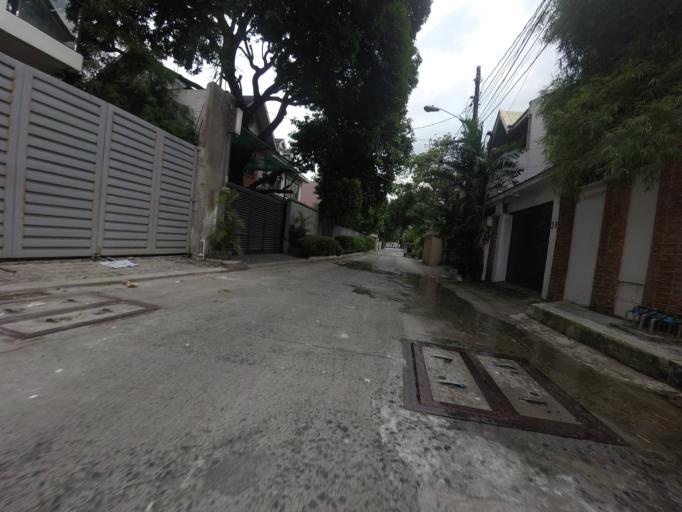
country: PH
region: Metro Manila
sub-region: San Juan
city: San Juan
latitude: 14.5953
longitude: 121.0417
